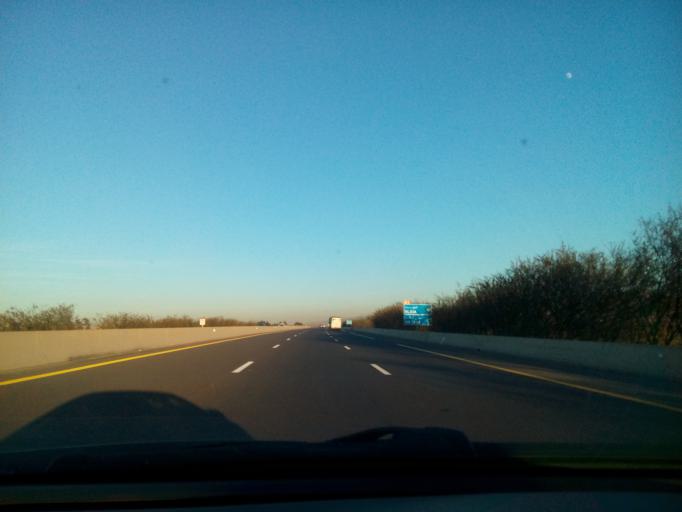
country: DZ
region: Relizane
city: Oued Rhiou
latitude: 35.9752
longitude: 0.9130
